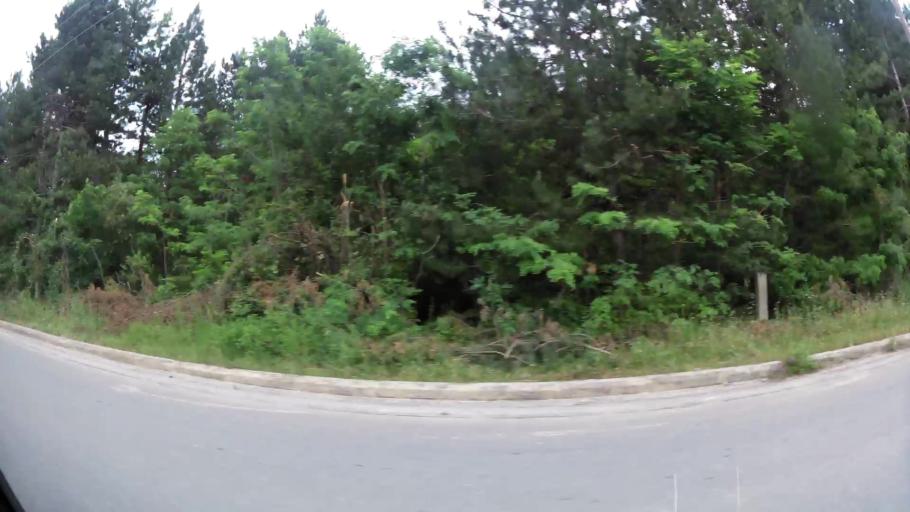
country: GR
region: West Macedonia
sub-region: Nomos Kozanis
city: Koila
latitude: 40.3321
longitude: 21.8268
